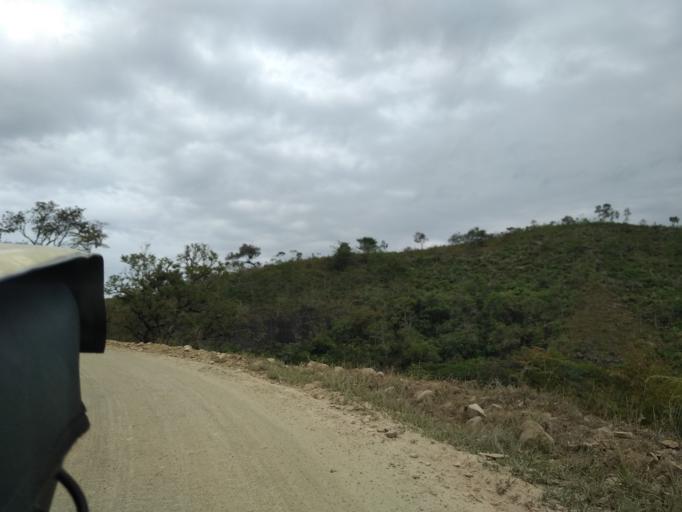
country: PE
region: Cajamarca
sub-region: Provincia de San Ignacio
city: Namballe
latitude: -4.9350
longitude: -79.1043
